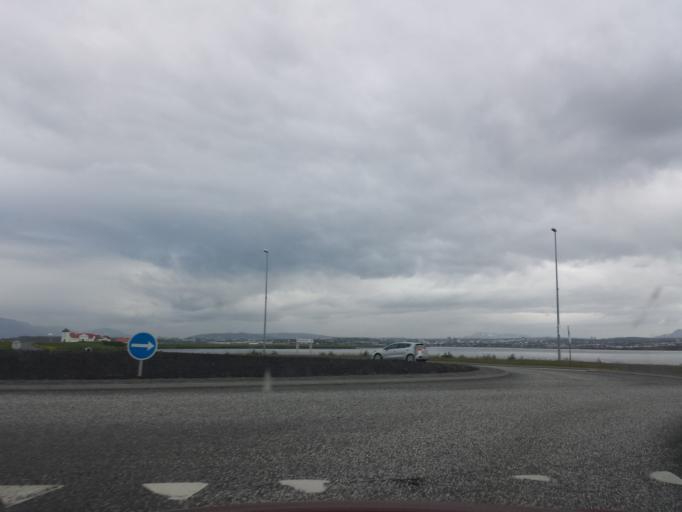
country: IS
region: Capital Region
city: Alftanes
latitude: 64.1019
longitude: -22.0101
